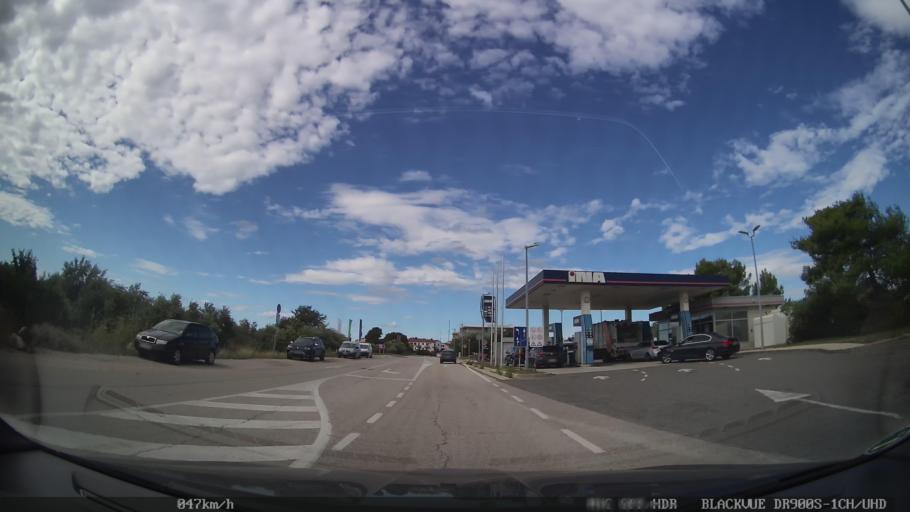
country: HR
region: Primorsko-Goranska
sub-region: Grad Krk
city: Krk
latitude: 45.0301
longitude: 14.5877
